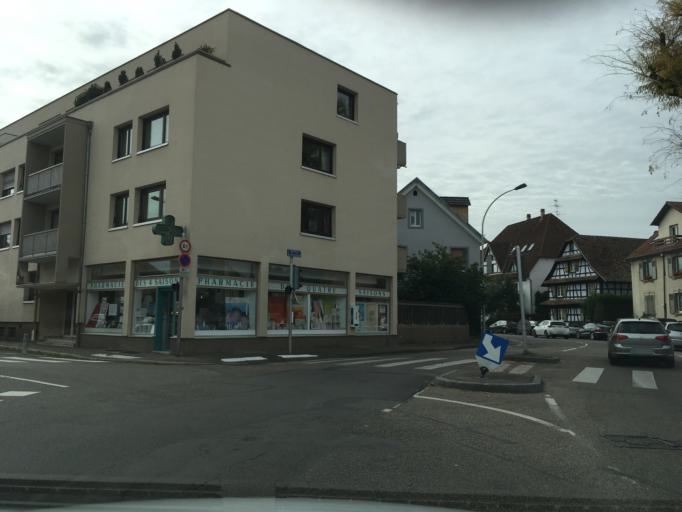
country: FR
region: Alsace
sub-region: Departement du Bas-Rhin
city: Bischheim
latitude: 48.6084
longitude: 7.7792
